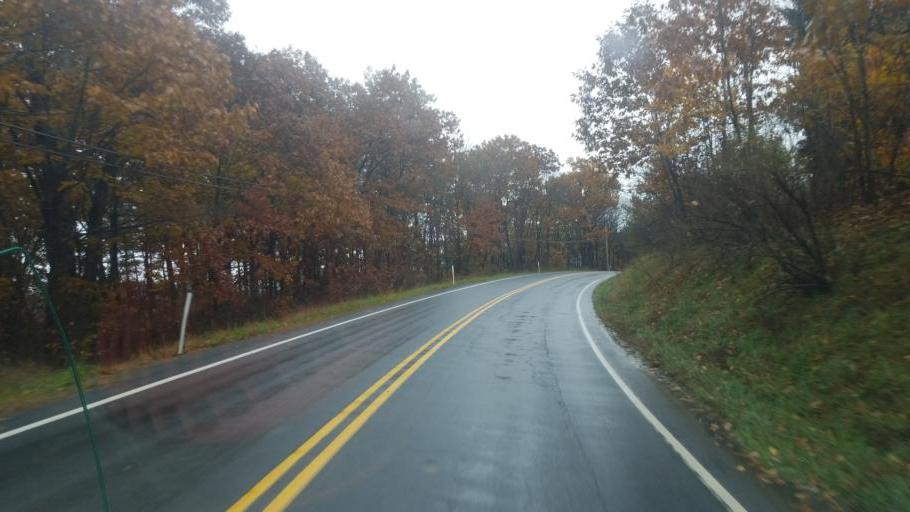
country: US
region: Pennsylvania
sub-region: Centre County
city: Milesburg
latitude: 41.0307
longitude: -77.9612
